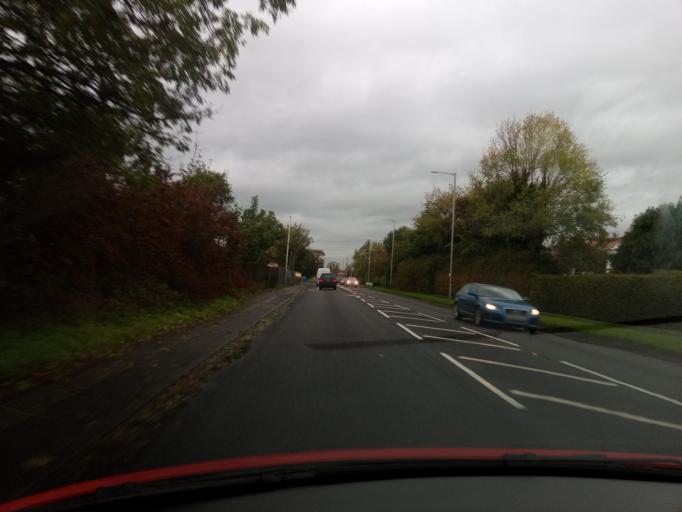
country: GB
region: England
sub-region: Lancashire
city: Catterall
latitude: 53.8343
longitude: -2.7385
